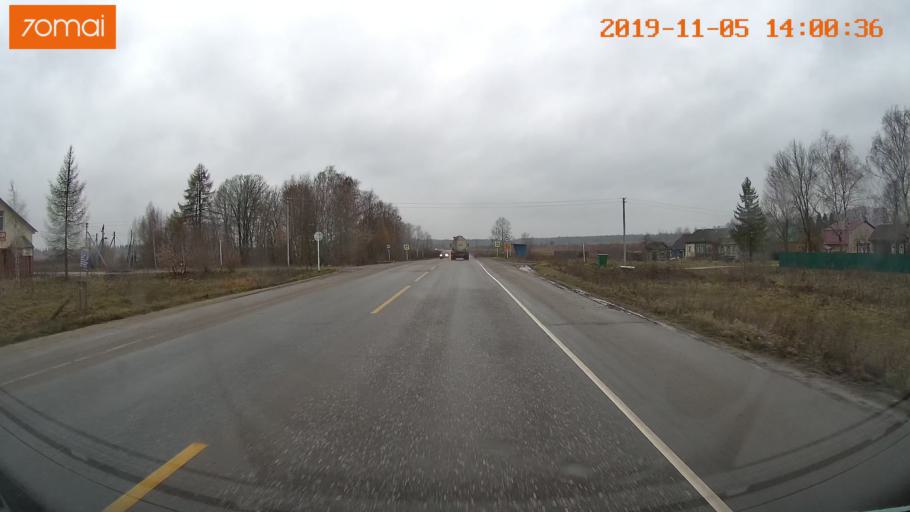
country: RU
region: Ivanovo
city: Kitovo
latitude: 57.0136
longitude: 41.2443
